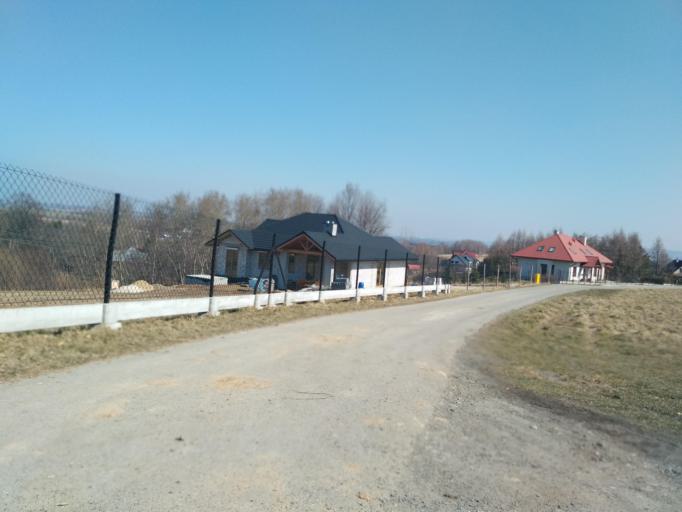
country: PL
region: Subcarpathian Voivodeship
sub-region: Powiat rzeszowski
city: Niechobrz
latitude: 49.9706
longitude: 21.8717
